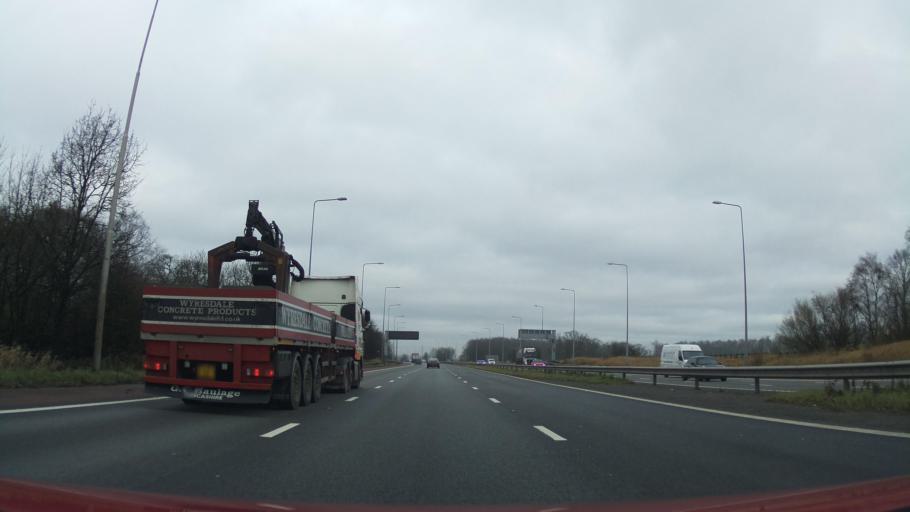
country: GB
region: England
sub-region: Lancashire
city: Coppull
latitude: 53.6085
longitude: -2.6886
